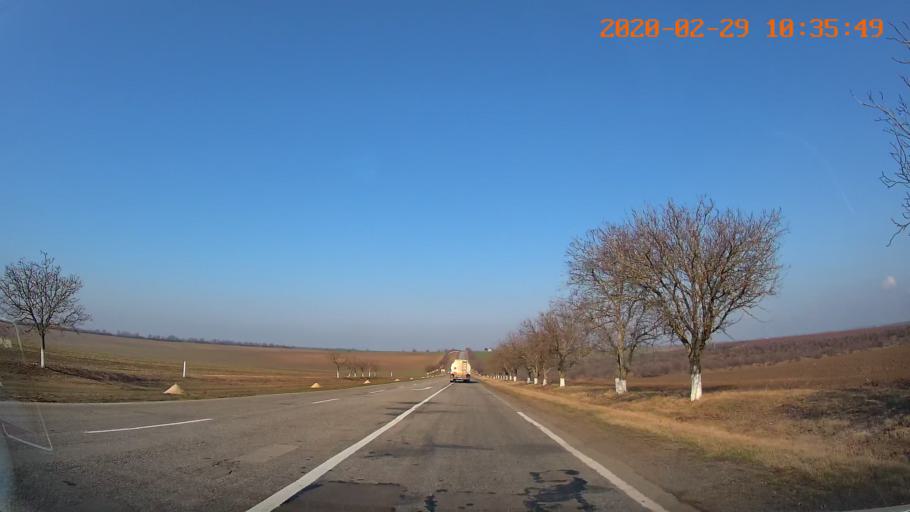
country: MD
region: Anenii Noi
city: Varnita
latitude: 46.9893
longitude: 29.5150
